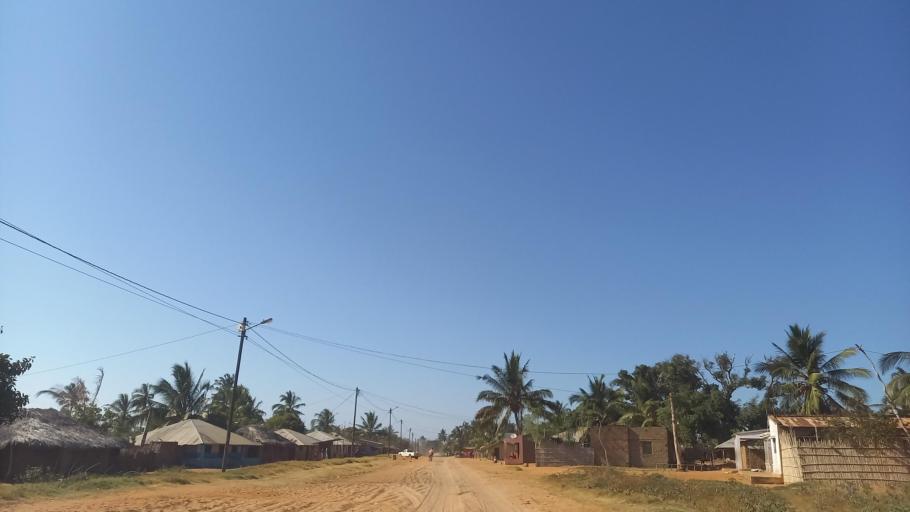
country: MZ
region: Cabo Delgado
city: Pemba
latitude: -13.1391
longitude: 40.5516
